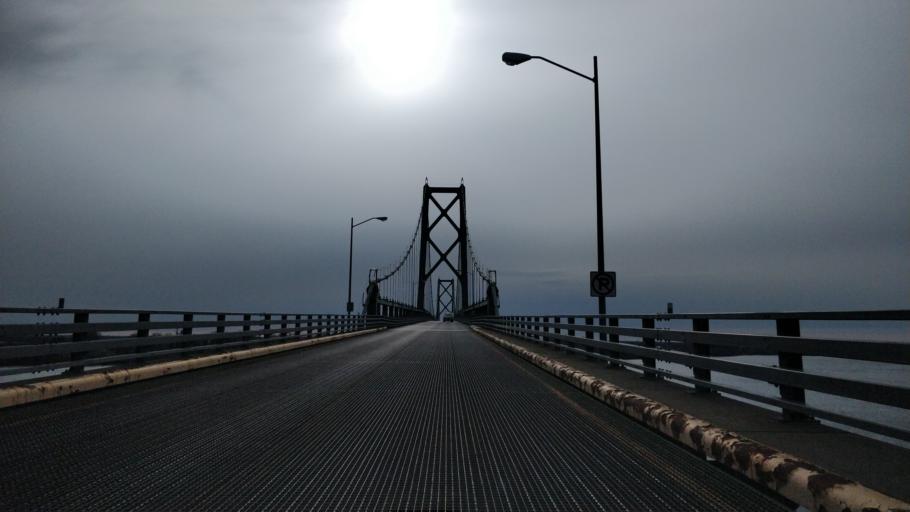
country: US
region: New York
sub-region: St. Lawrence County
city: Ogdensburg
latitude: 44.7384
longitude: -75.4619
